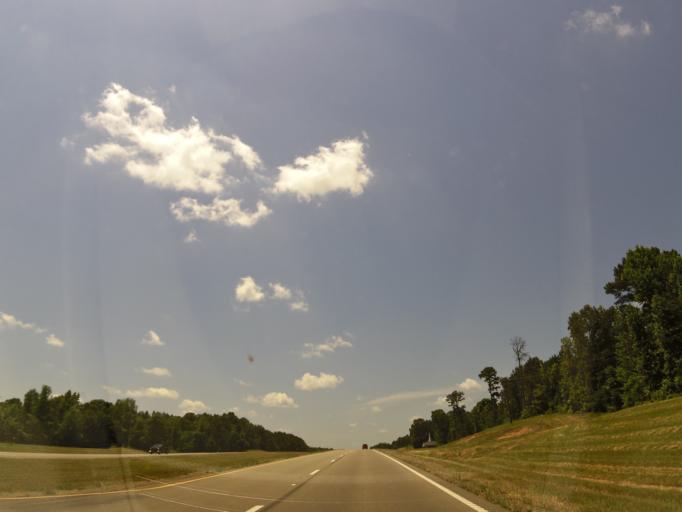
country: US
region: Mississippi
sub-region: Pontotoc County
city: Pontotoc
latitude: 34.2936
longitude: -89.2080
